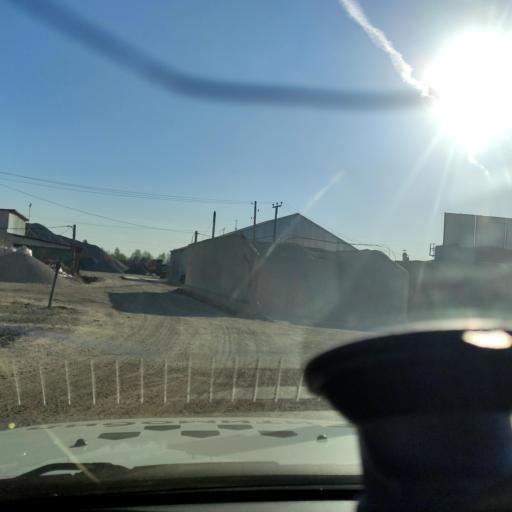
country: RU
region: Perm
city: Gamovo
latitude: 57.9055
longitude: 56.1800
